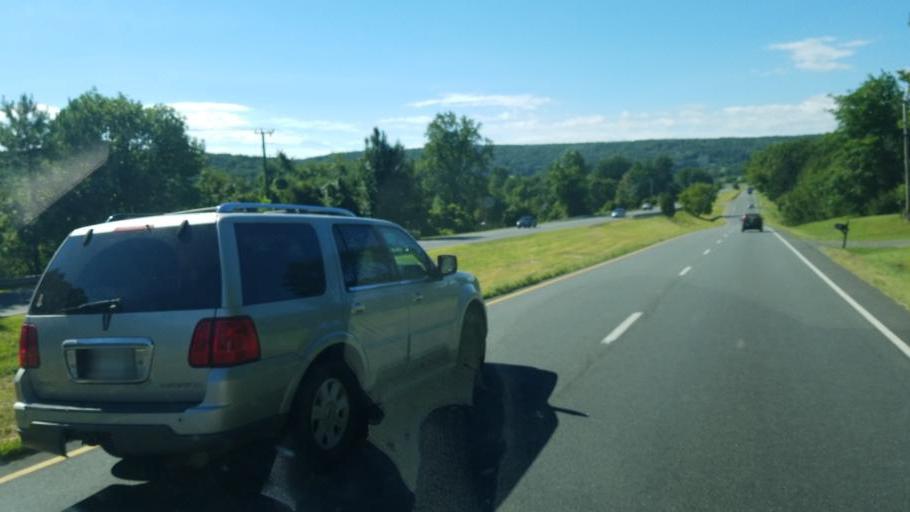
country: US
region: Virginia
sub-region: Fauquier County
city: Marshall
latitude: 38.8161
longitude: -77.8135
